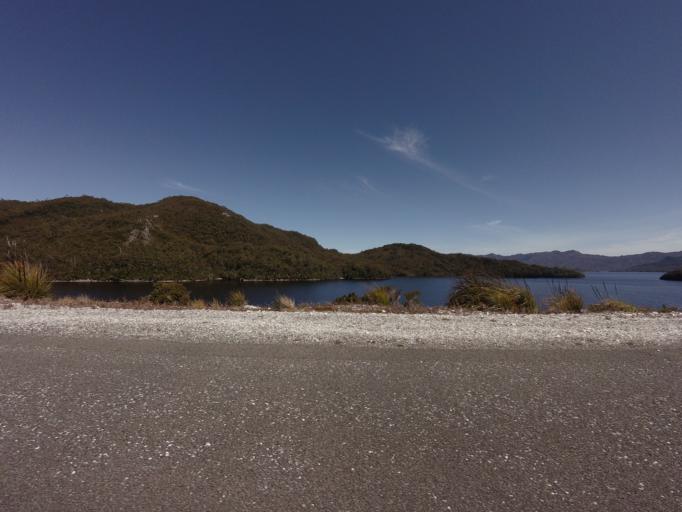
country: AU
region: Tasmania
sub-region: West Coast
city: Queenstown
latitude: -42.7971
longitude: 146.0727
